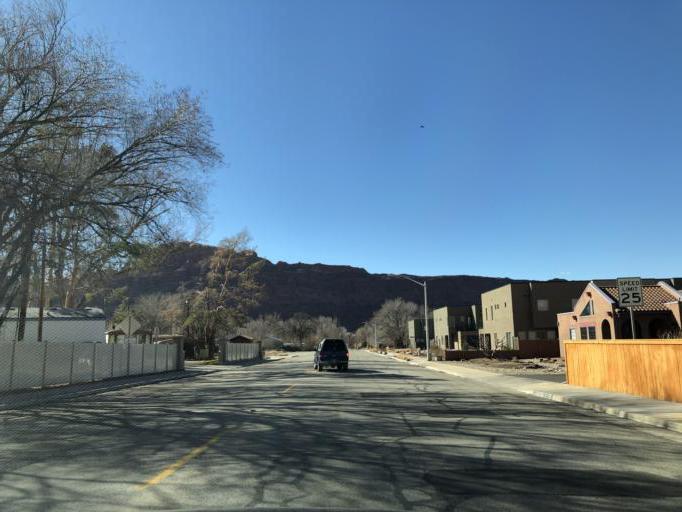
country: US
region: Utah
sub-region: Grand County
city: Moab
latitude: 38.5794
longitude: -109.5619
